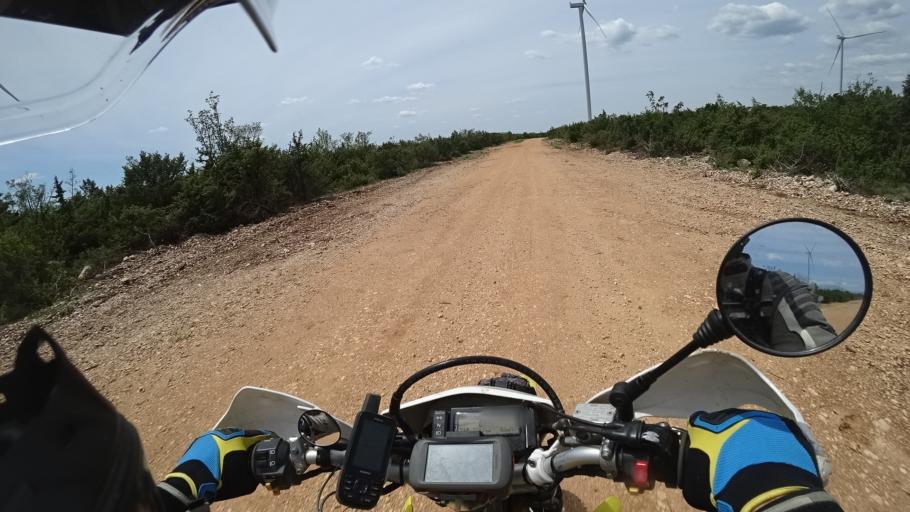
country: HR
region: Sibensko-Kniniska
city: Knin
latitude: 44.0599
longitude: 16.0737
